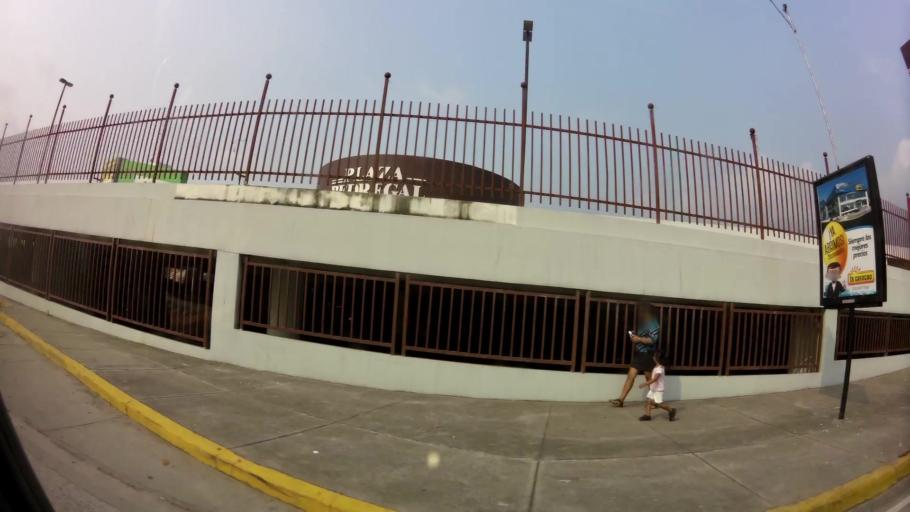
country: HN
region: Cortes
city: El Zapotal del Norte
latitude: 15.5248
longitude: -88.0381
